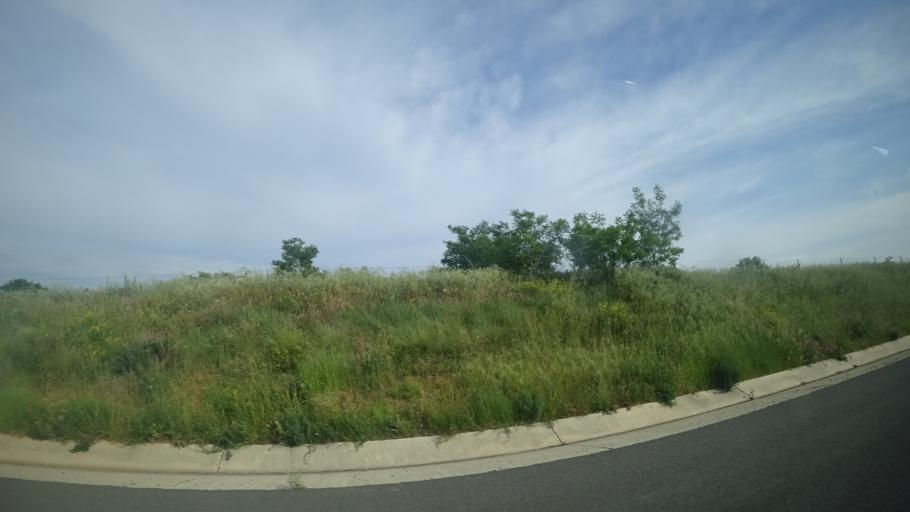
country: FR
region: Languedoc-Roussillon
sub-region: Departement de l'Herault
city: Servian
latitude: 43.3891
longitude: 3.3180
